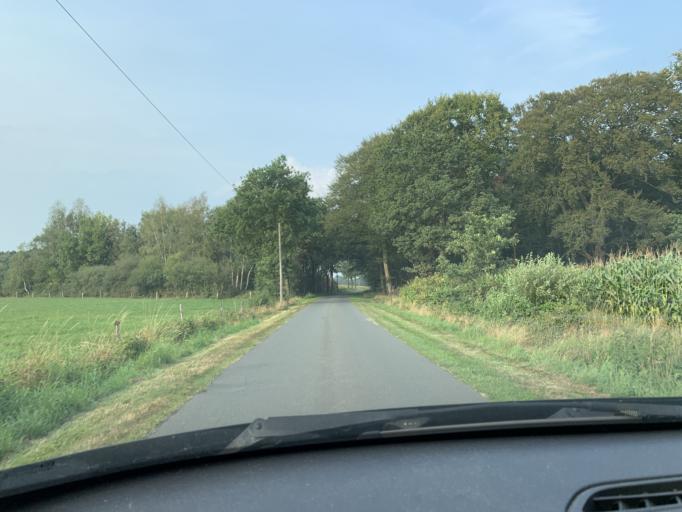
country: DE
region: Lower Saxony
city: Apen
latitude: 53.2525
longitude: 7.8395
